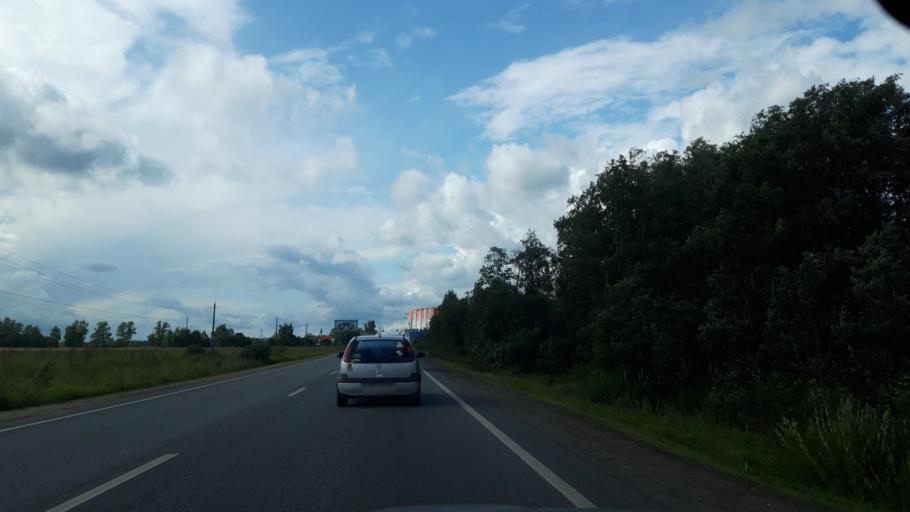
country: RU
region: Moskovskaya
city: Andreyevka
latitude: 55.9681
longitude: 37.1006
